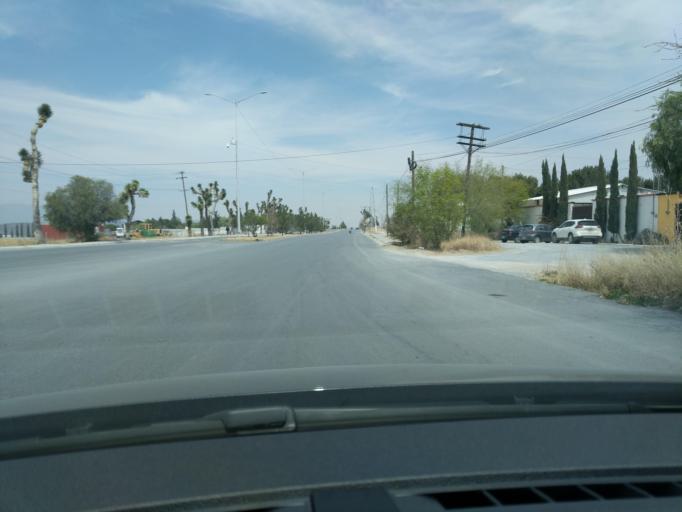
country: MX
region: Coahuila
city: Saltillo
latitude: 25.3571
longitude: -101.0314
